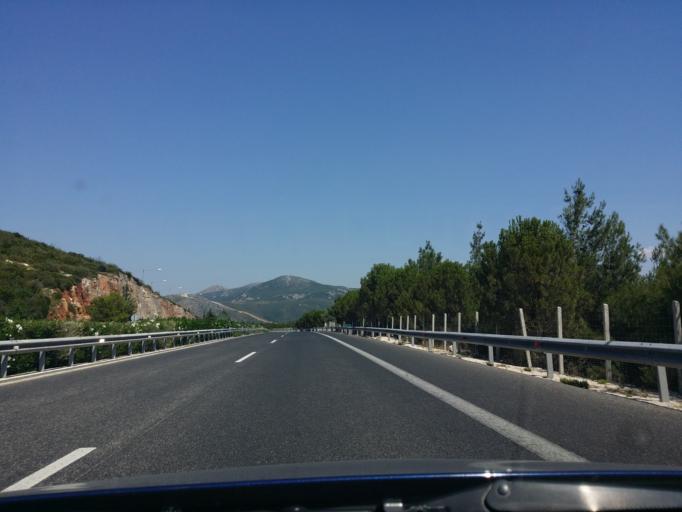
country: GR
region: Peloponnese
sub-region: Nomos Korinthias
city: Nemea
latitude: 37.7832
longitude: 22.6946
